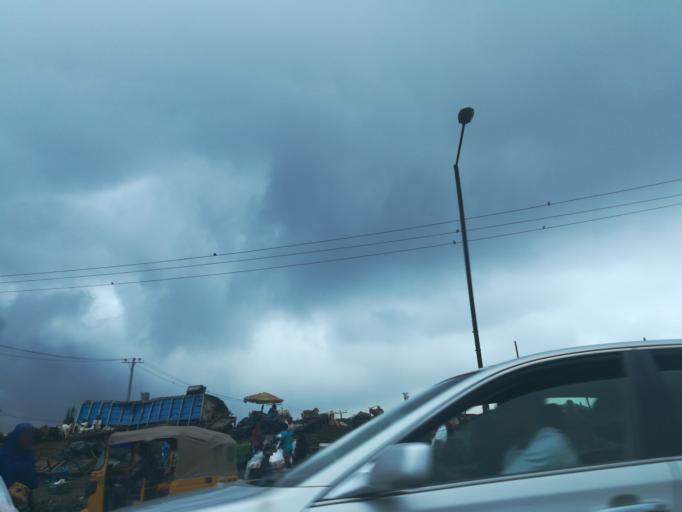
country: NG
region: Lagos
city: Agege
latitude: 6.6130
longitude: 3.3283
